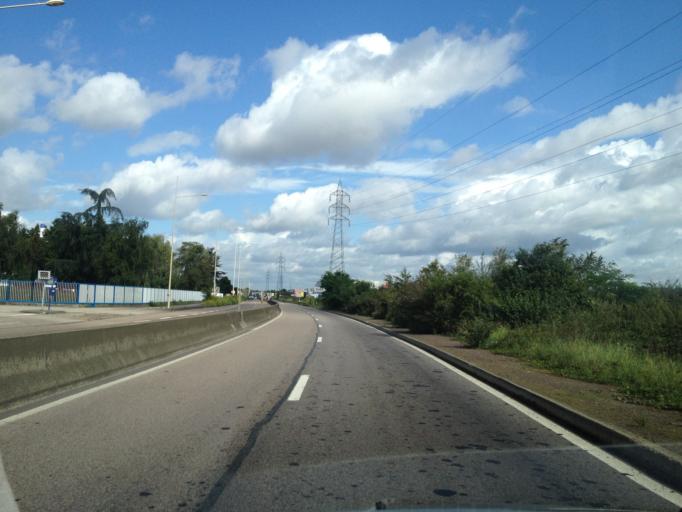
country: FR
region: Haute-Normandie
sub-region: Departement de la Seine-Maritime
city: Saint-Etienne-du-Rouvray
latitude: 49.3734
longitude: 1.1156
